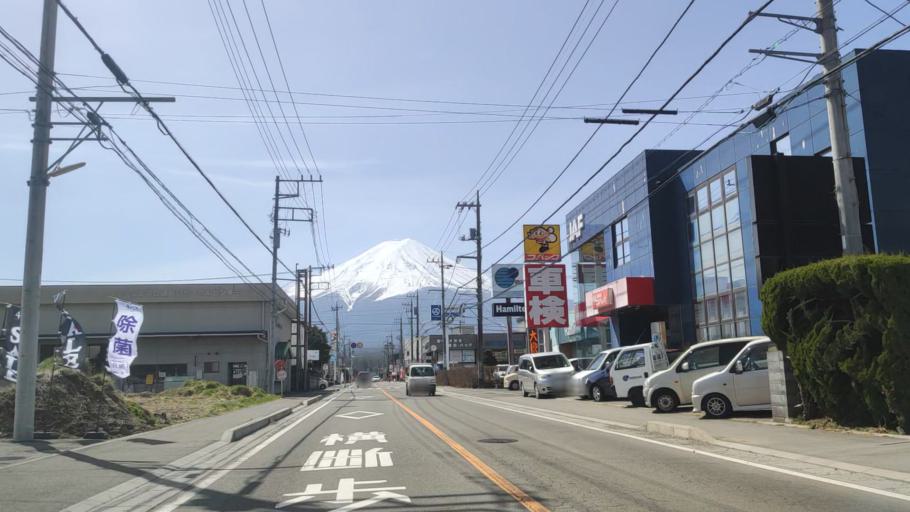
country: JP
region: Yamanashi
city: Fujikawaguchiko
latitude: 35.4931
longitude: 138.7638
